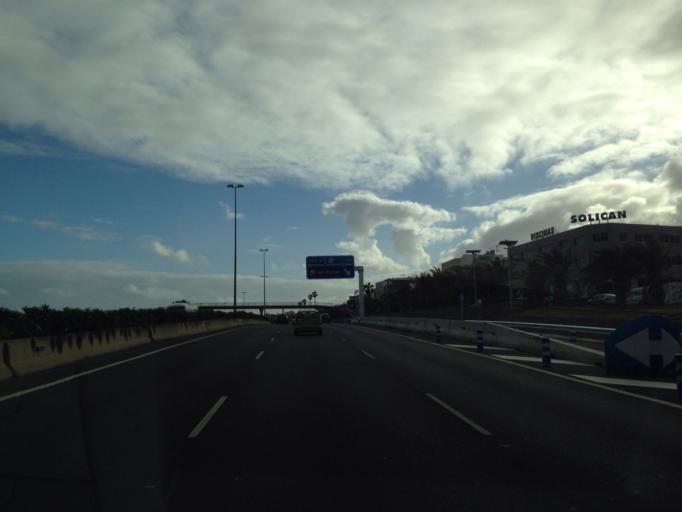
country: ES
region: Canary Islands
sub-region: Provincia de Las Palmas
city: Telde
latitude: 27.9871
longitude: -15.3925
